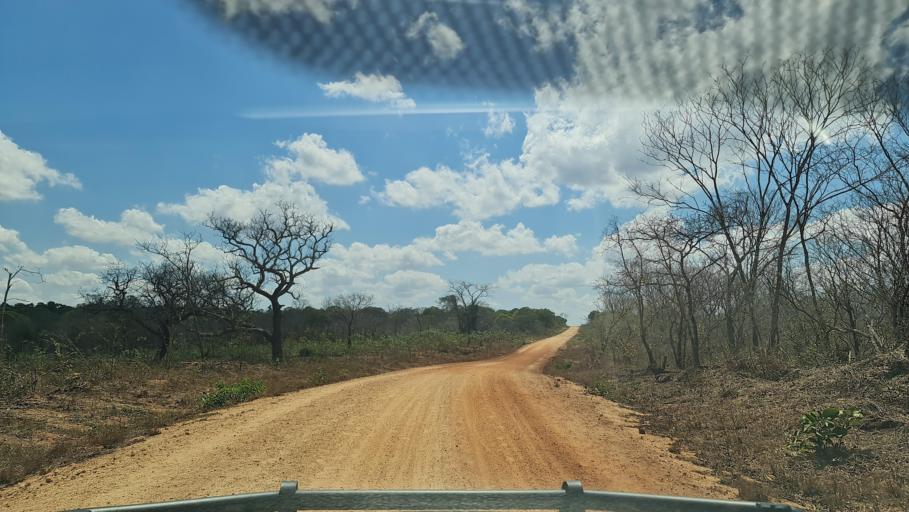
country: MZ
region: Nampula
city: Nacala
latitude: -14.1770
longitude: 40.2265
